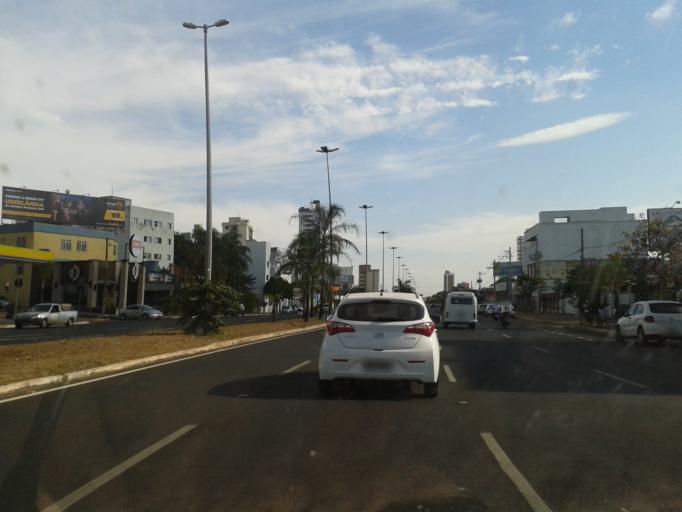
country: BR
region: Minas Gerais
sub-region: Uberlandia
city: Uberlandia
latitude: -18.9144
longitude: -48.2624
